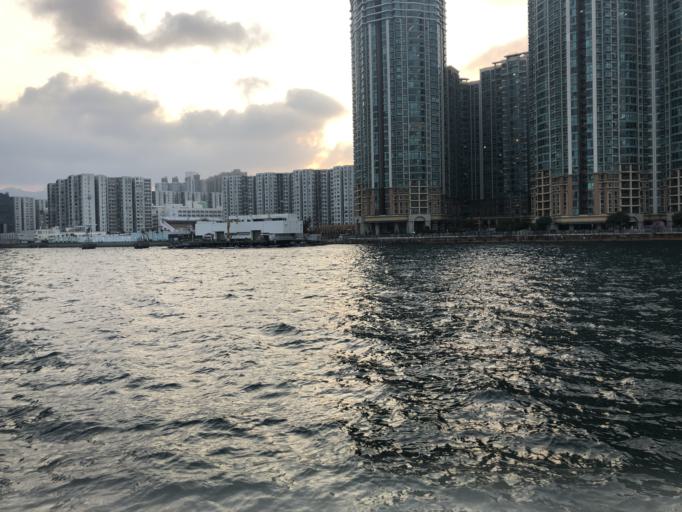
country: HK
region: Kowloon City
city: Kowloon
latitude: 22.3071
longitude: 114.1955
